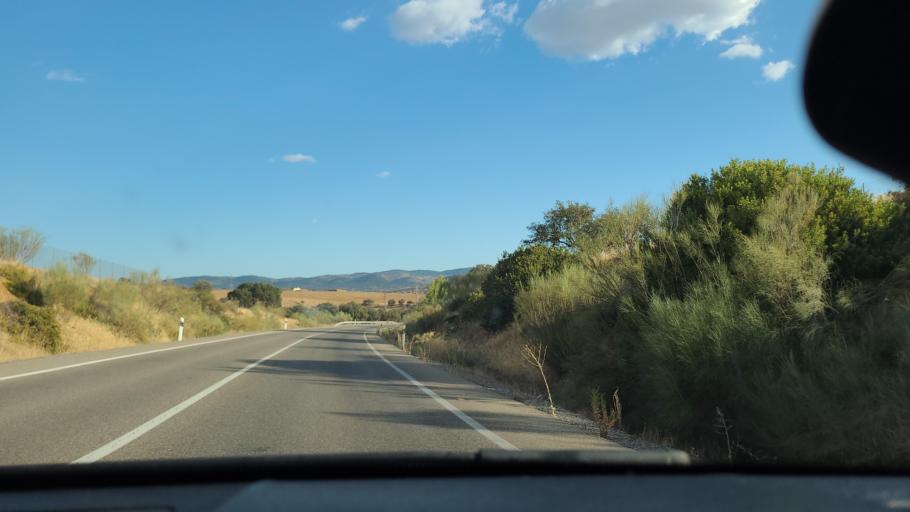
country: ES
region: Andalusia
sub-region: Province of Cordoba
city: Belmez
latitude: 38.2532
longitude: -5.1684
